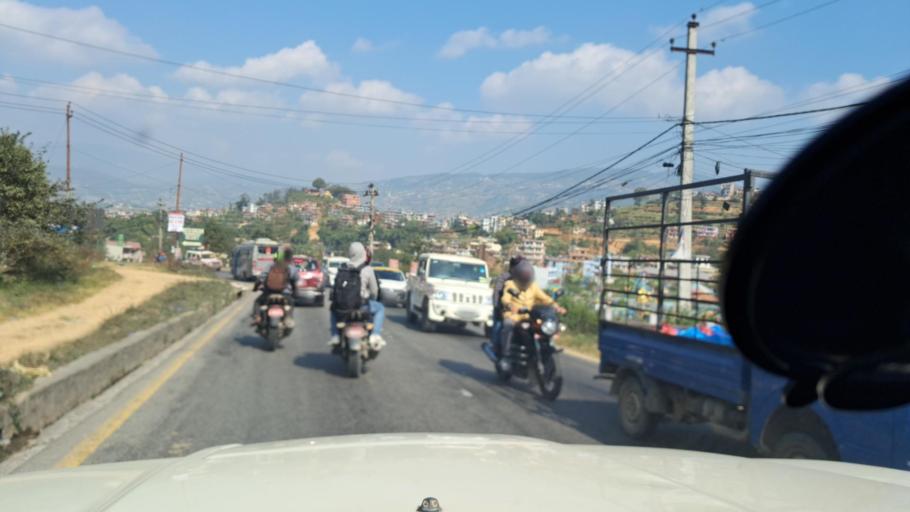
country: NP
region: Central Region
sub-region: Bagmati Zone
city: kankrabari Dovan
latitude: 27.6456
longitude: 85.4656
